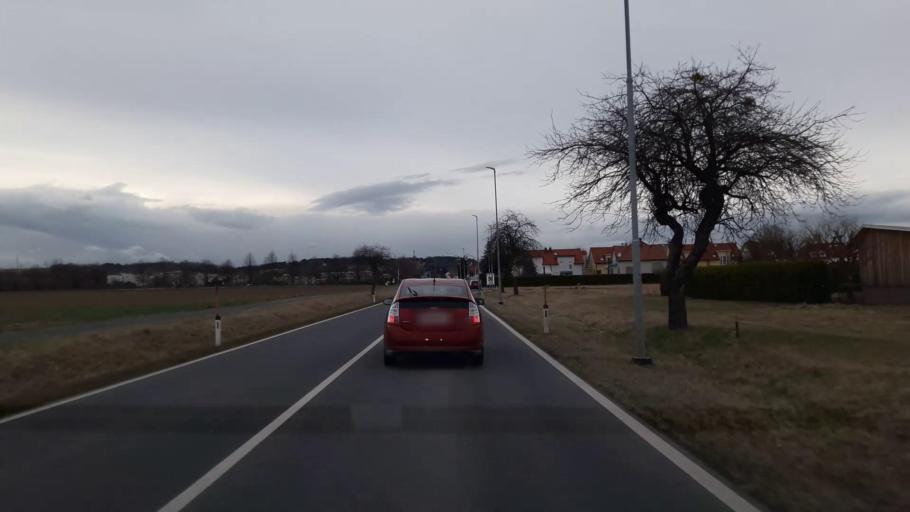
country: AT
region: Burgenland
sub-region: Politischer Bezirk Oberpullendorf
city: Oberpullendorf
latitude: 47.4903
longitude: 16.5184
